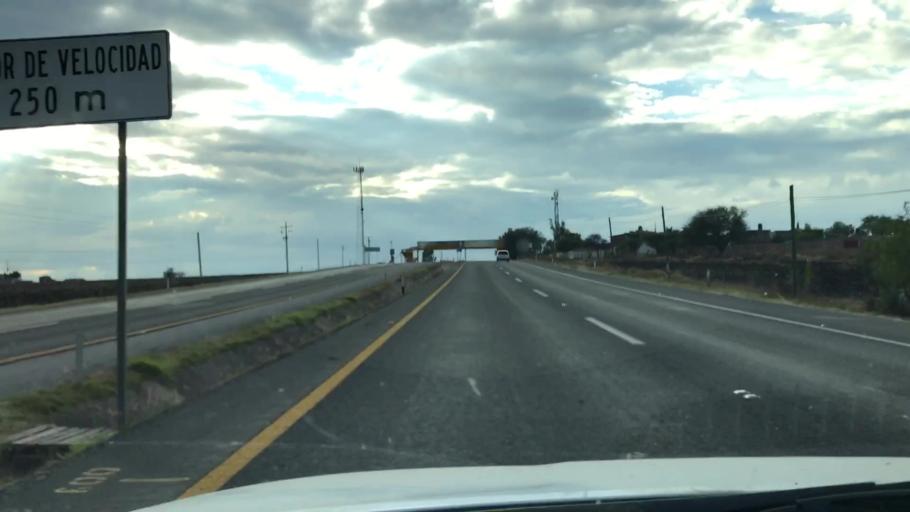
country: MX
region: Guanajuato
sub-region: Penjamo
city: Mezquite de Luna
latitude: 20.3797
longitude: -101.8327
